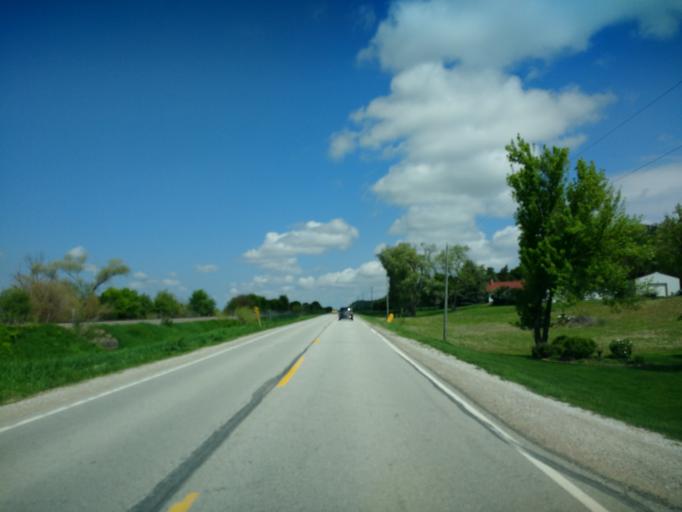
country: US
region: Iowa
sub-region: Harrison County
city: Missouri Valley
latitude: 41.4577
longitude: -95.8754
